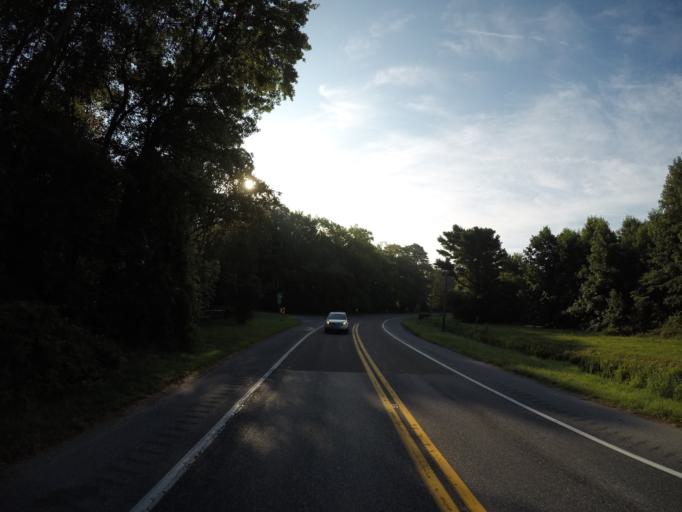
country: US
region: Delaware
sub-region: Sussex County
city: Selbyville
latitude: 38.5146
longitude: -75.1803
